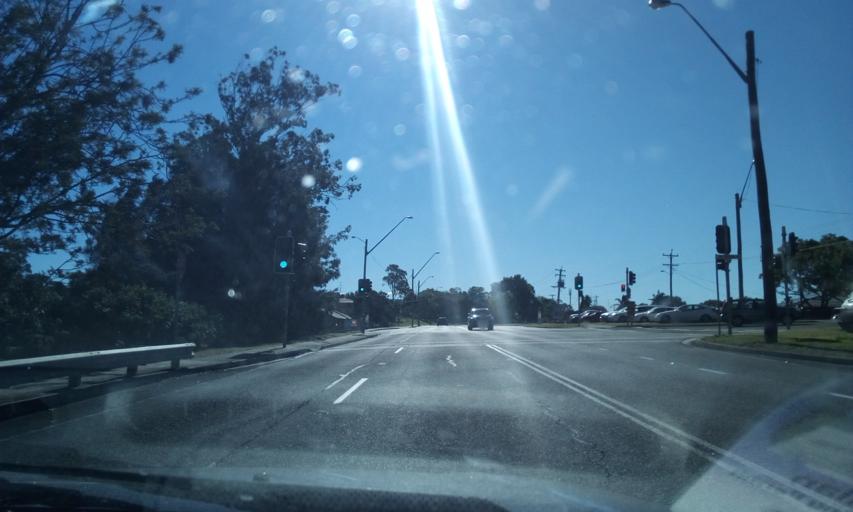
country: AU
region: New South Wales
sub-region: Wollongong
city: Dapto
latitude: -34.5132
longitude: 150.7843
